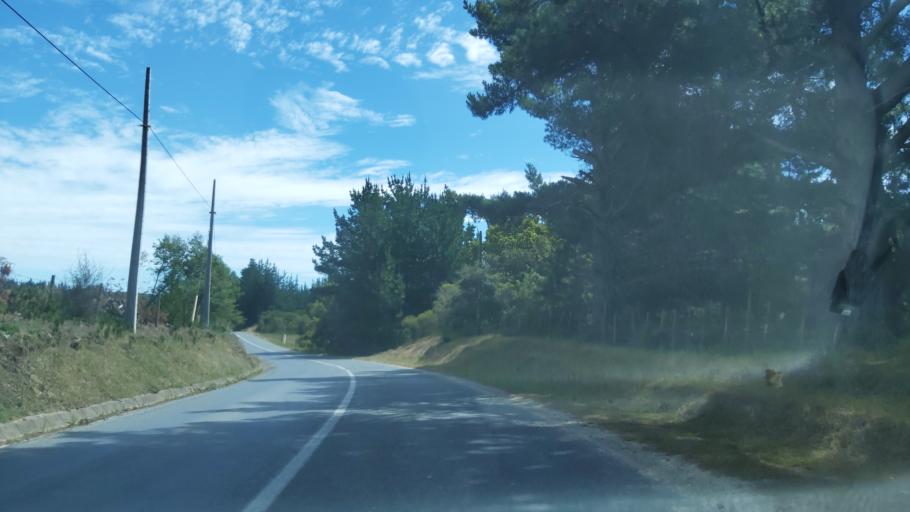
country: CL
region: Maule
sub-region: Provincia de Talca
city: Constitucion
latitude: -35.5398
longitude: -72.5557
